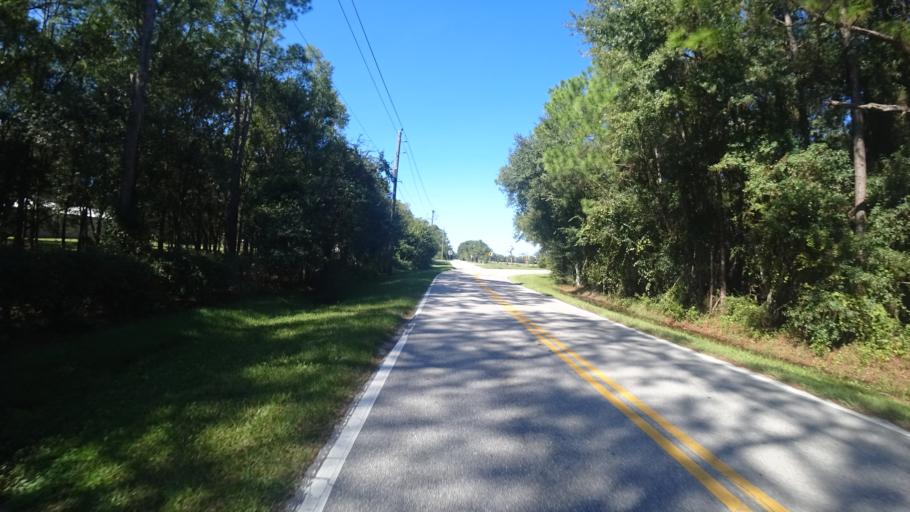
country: US
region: Florida
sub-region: Sarasota County
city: Lake Sarasota
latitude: 27.3204
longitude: -82.2683
